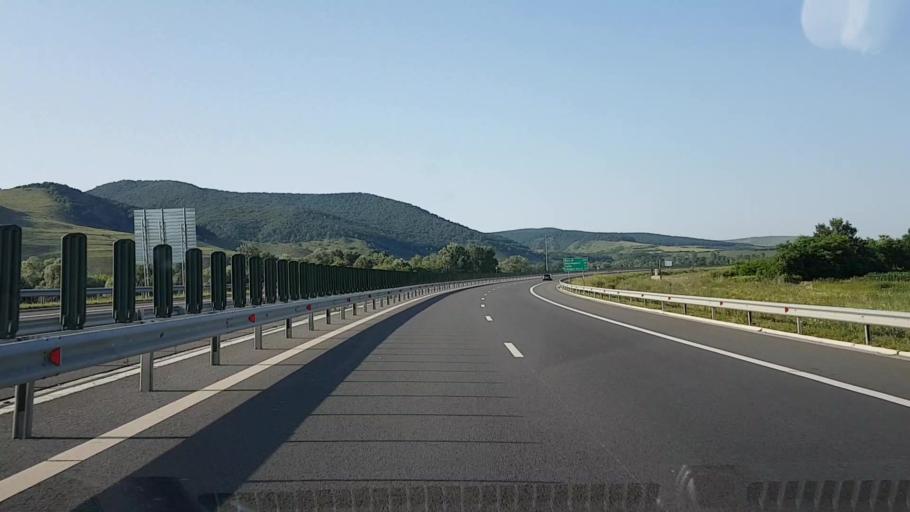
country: RO
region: Alba
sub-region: Comuna Miraslau
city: Miraslau
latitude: 46.3541
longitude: 23.7240
